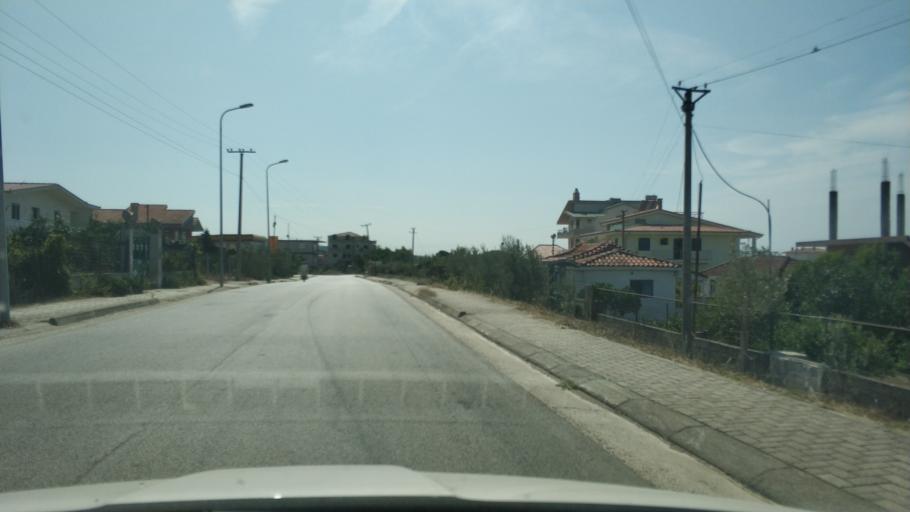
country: AL
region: Fier
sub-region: Rrethi i Lushnjes
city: Divjake
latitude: 40.9792
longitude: 19.5353
